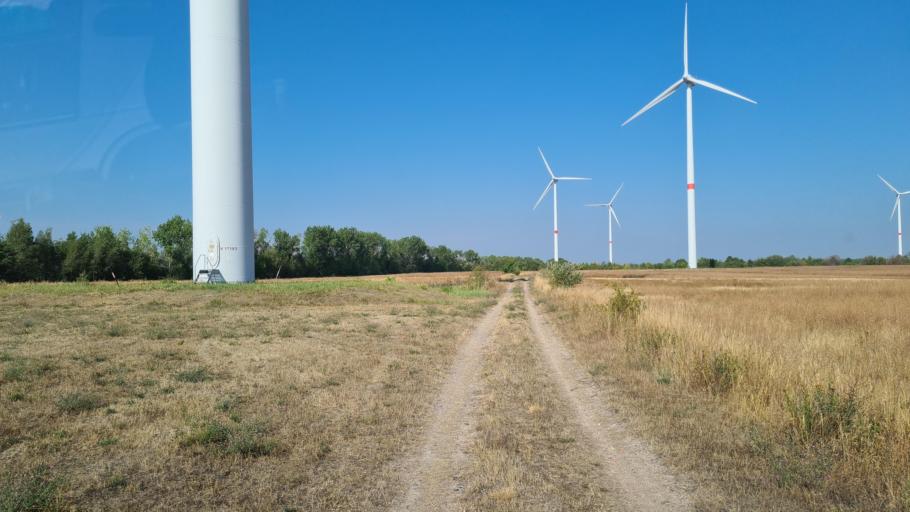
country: DE
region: Brandenburg
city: Sallgast
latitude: 51.5525
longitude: 13.8367
